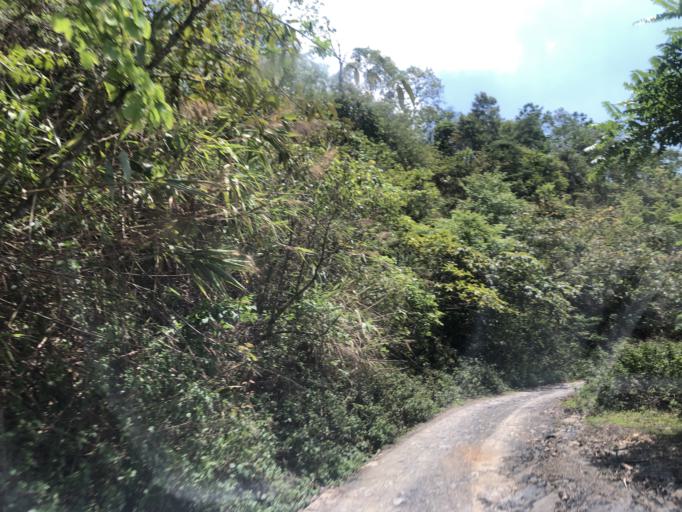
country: LA
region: Phongsali
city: Phongsali
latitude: 21.4427
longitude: 102.1636
